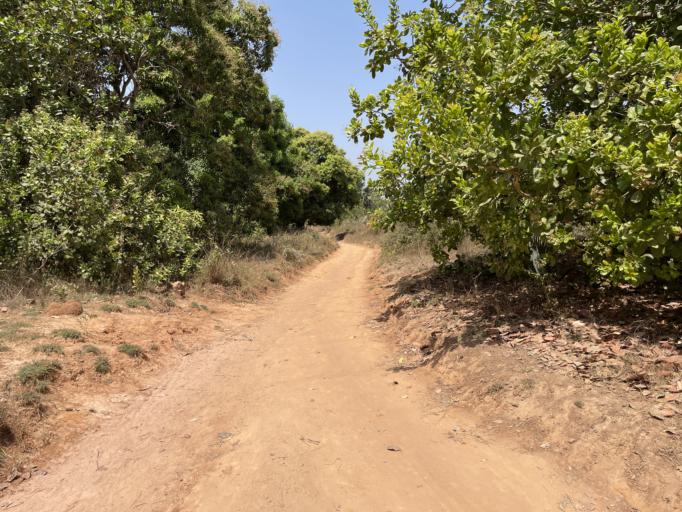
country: GW
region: Oio
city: Bissora
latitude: 12.4382
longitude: -15.6153
